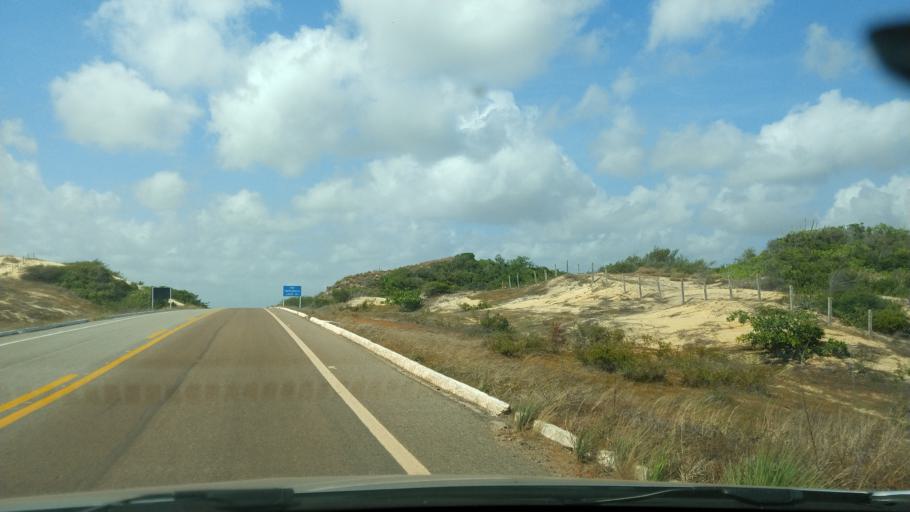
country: BR
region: Rio Grande do Norte
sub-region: Touros
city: Touros
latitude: -5.1621
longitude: -35.5023
